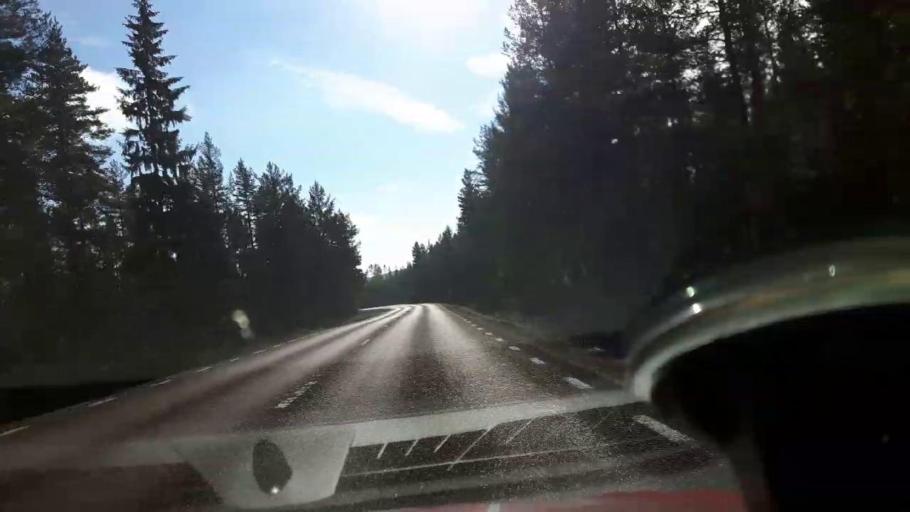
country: SE
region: Gaevleborg
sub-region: Ljusdals Kommun
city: Farila
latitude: 61.9035
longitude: 15.6385
